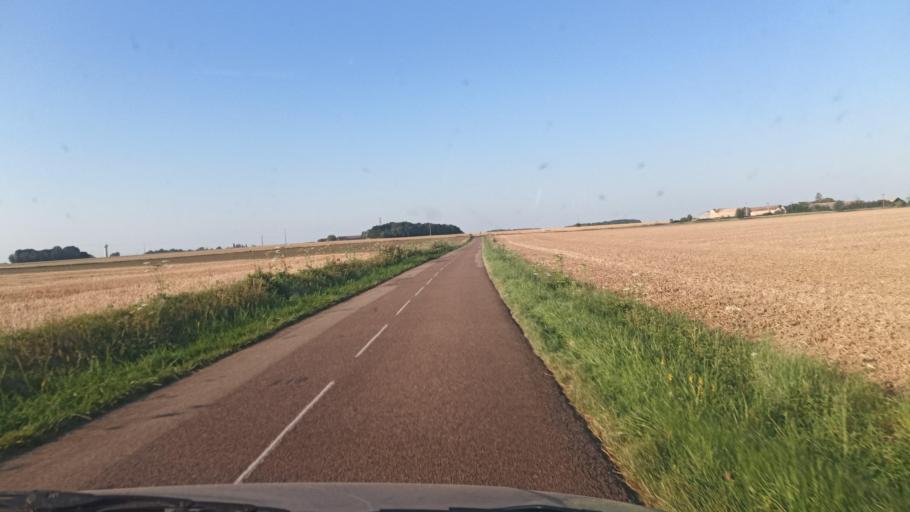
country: FR
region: Bourgogne
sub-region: Departement de l'Yonne
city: Saint-Valerien
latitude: 48.2128
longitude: 3.1214
